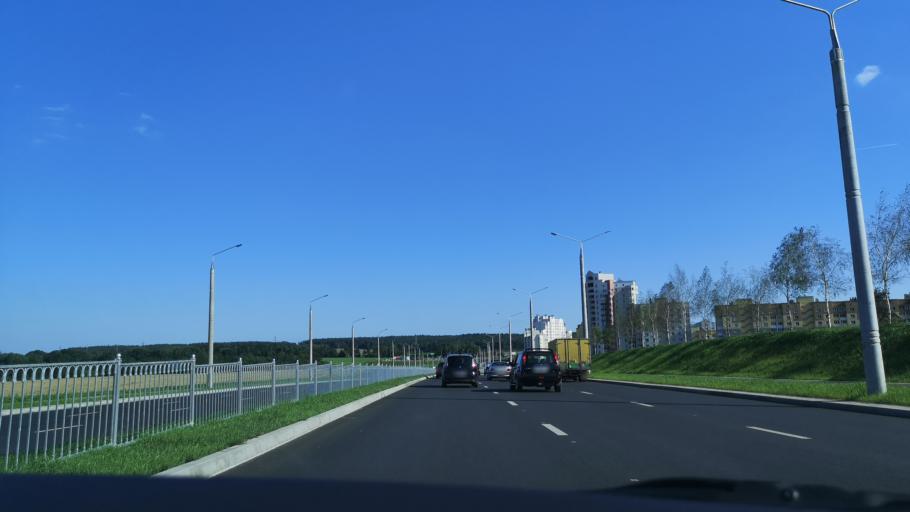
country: BY
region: Grodnenskaya
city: Hrodna
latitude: 53.6489
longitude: 23.8625
